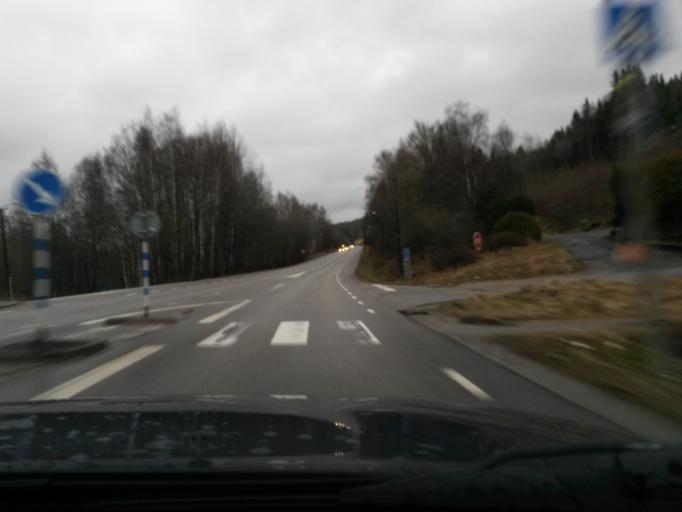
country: SE
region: Vaestra Goetaland
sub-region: Boras Kommun
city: Boras
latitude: 57.7768
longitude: 12.9815
